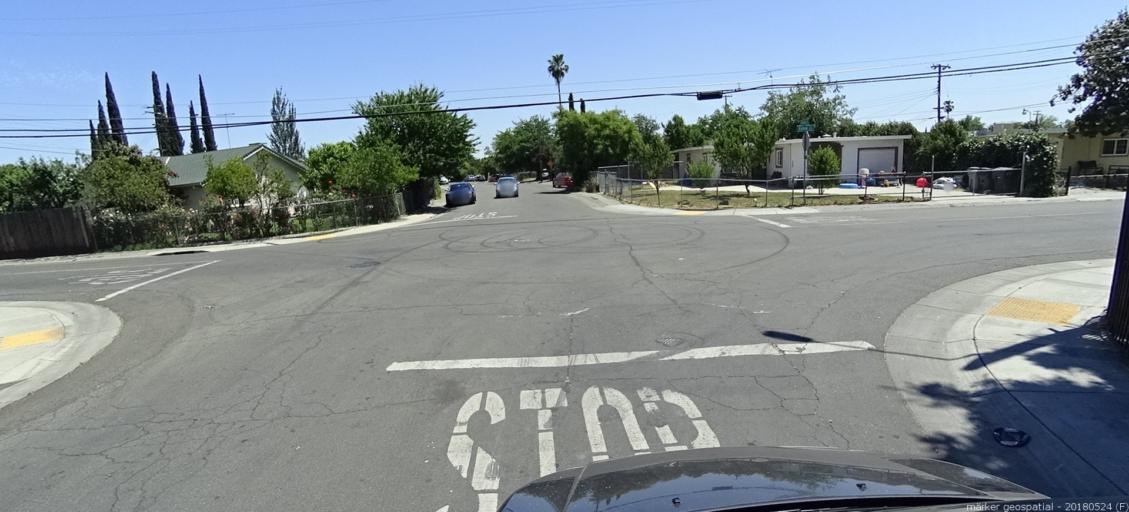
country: US
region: California
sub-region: Sacramento County
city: Sacramento
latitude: 38.6204
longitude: -121.4596
